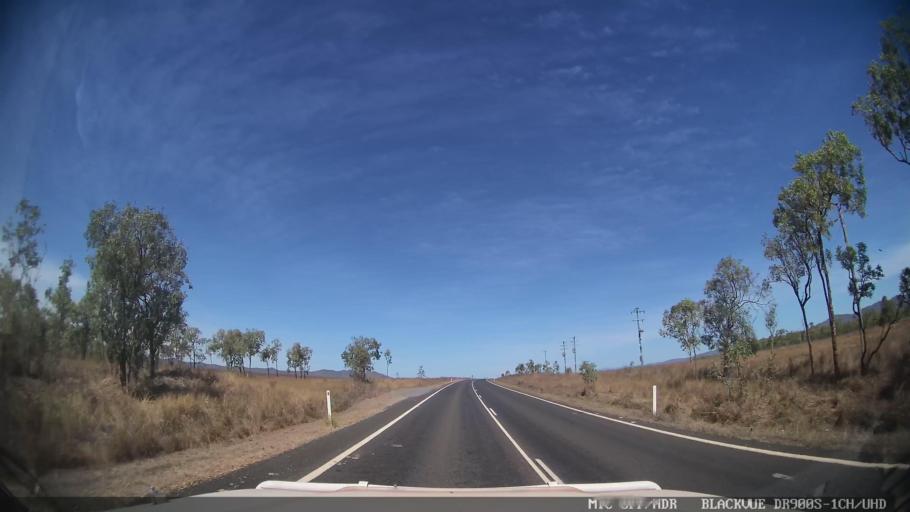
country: AU
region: Queensland
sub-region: Cook
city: Cooktown
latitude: -15.7916
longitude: 144.7085
